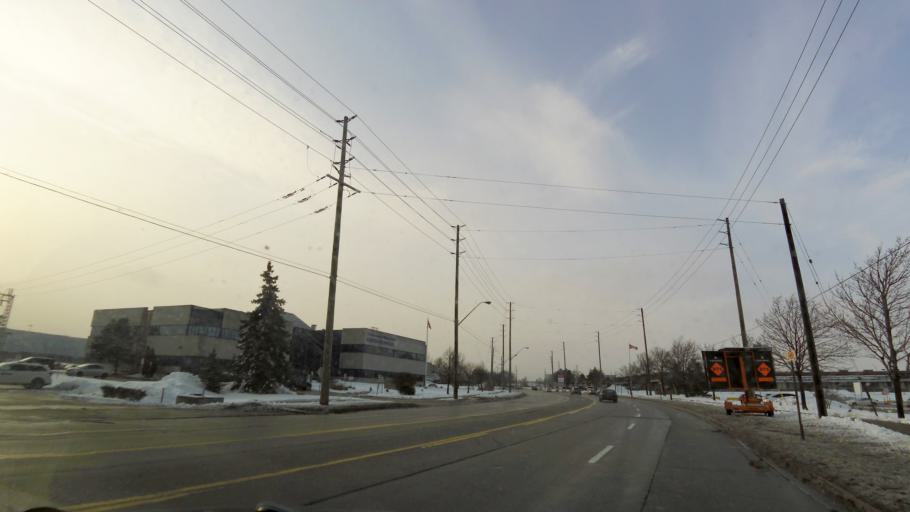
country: CA
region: Ontario
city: Brampton
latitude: 43.7031
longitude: -79.7238
